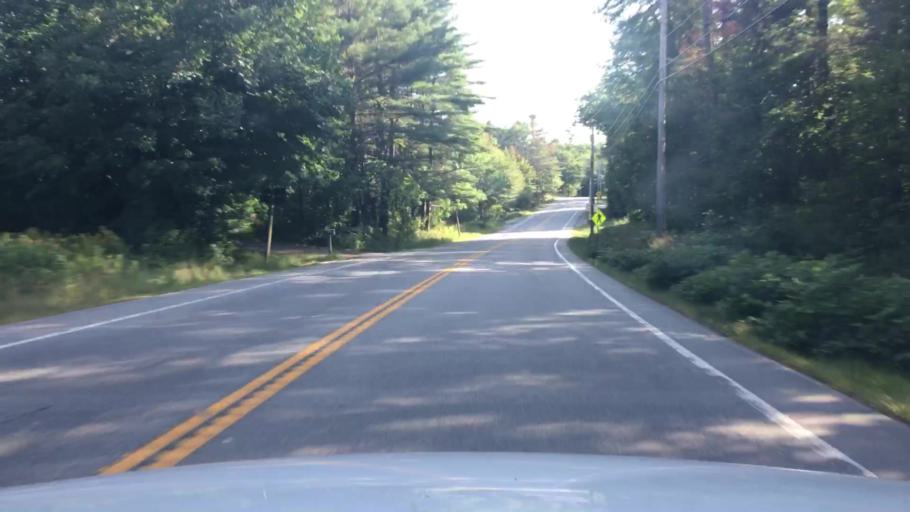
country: US
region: Maine
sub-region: Cumberland County
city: New Gloucester
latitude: 43.9392
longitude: -70.3035
